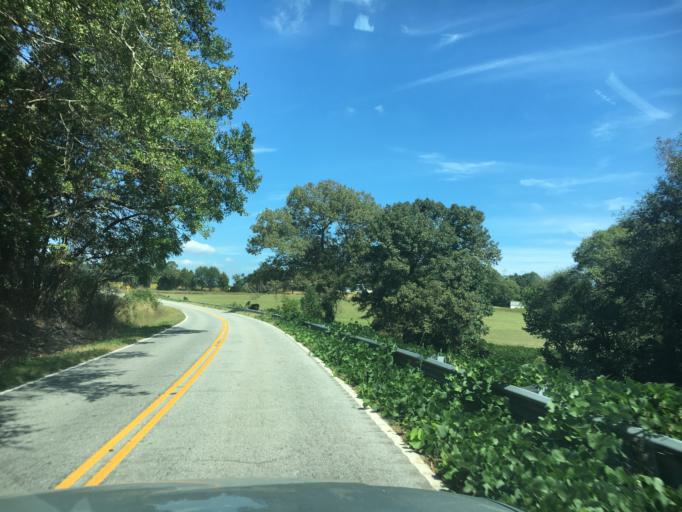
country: US
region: South Carolina
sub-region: Spartanburg County
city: Mayo
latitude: 35.1151
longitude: -81.9149
